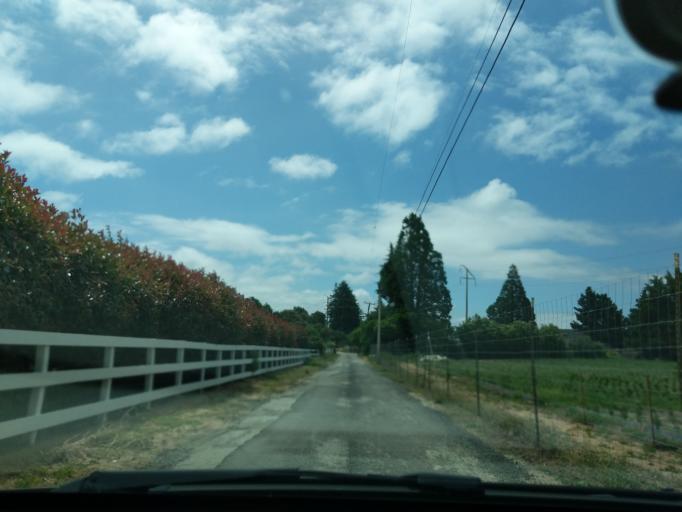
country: US
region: California
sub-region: Santa Cruz County
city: Aptos Hills-Larkin Valley
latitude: 36.9477
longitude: -121.8139
